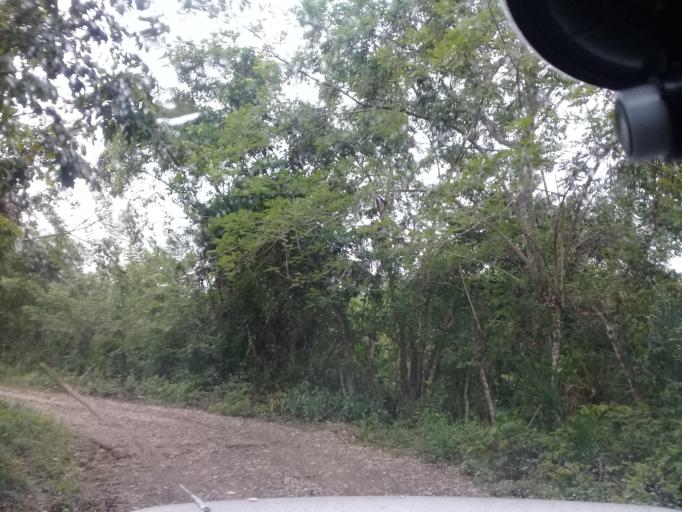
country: MX
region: Veracruz
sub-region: Chalma
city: San Pedro Coyutla
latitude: 21.2470
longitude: -98.4153
